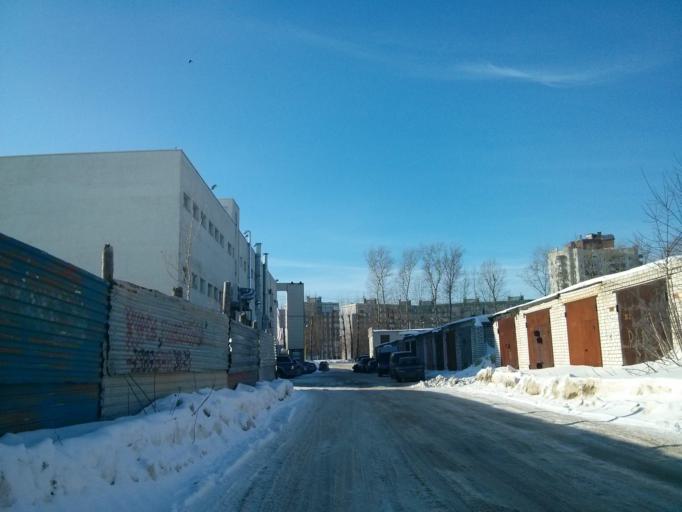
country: RU
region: Nizjnij Novgorod
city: Afonino
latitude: 56.2887
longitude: 44.0785
